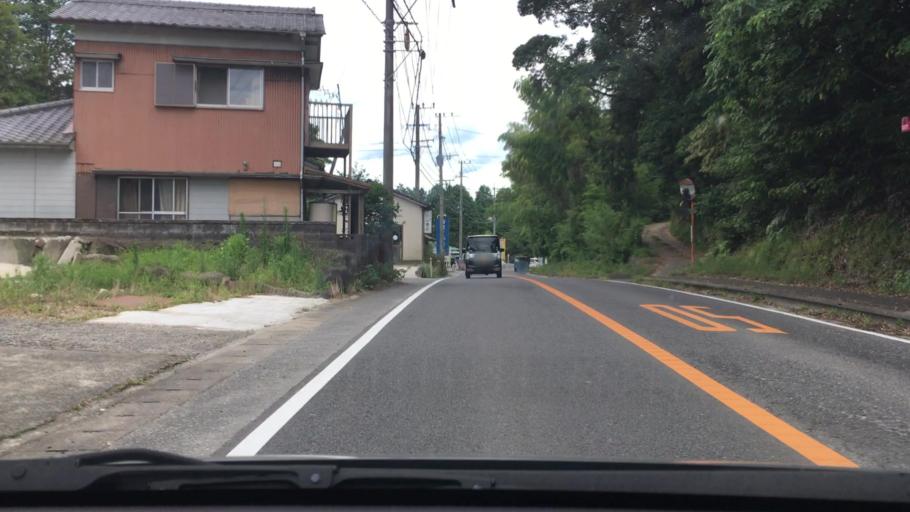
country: JP
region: Nagasaki
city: Togitsu
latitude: 32.9807
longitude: 129.7815
